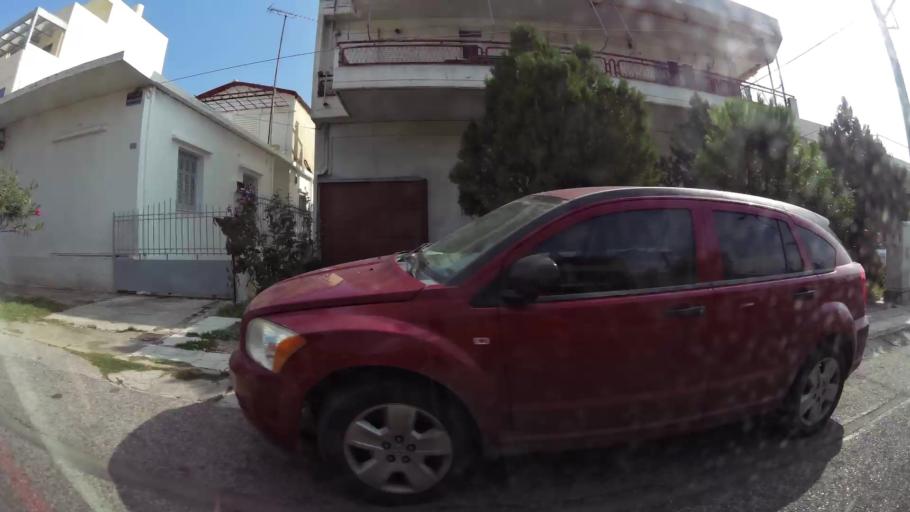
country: GR
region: Attica
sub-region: Nomarchia Dytikis Attikis
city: Zefyri
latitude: 38.0597
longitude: 23.7315
